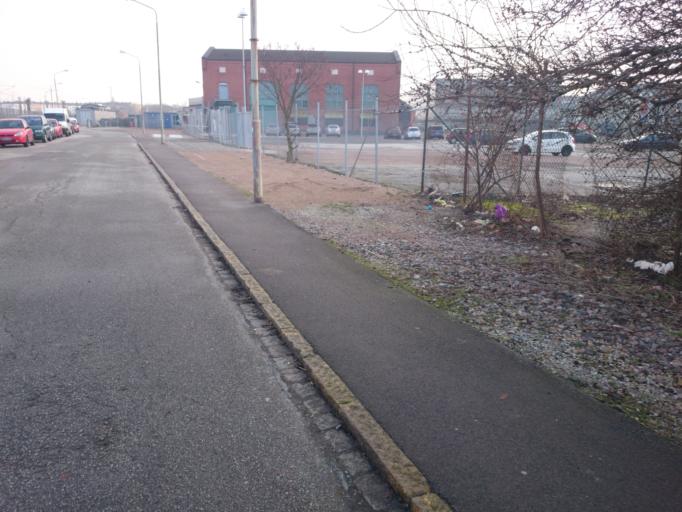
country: SE
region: Skane
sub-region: Malmo
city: Malmoe
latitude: 55.6094
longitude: 13.0202
